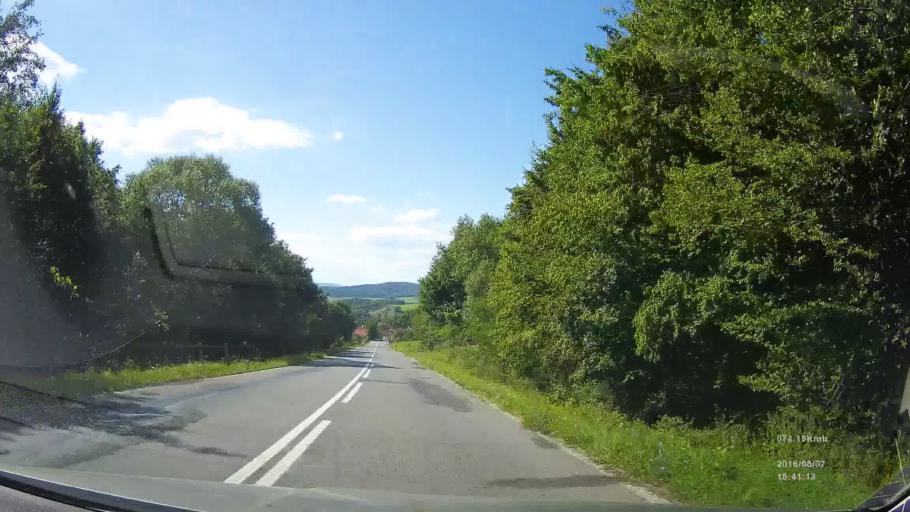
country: SK
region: Presovsky
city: Giraltovce
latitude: 49.1233
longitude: 21.5810
